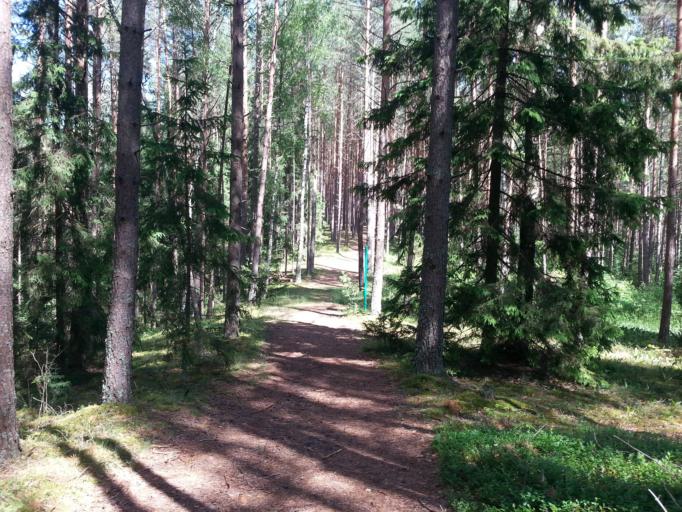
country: BY
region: Vitebsk
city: Lyntupy
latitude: 54.9662
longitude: 26.3794
